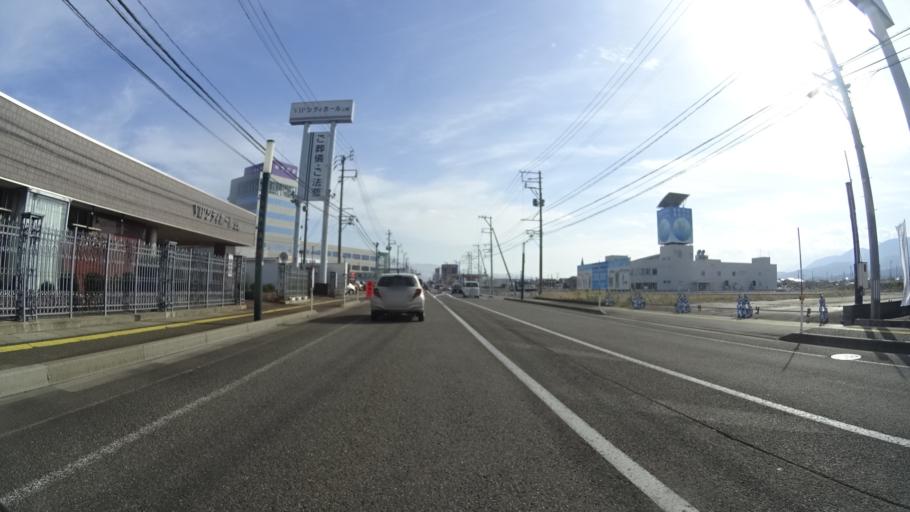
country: JP
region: Niigata
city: Joetsu
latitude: 37.1324
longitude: 138.2442
